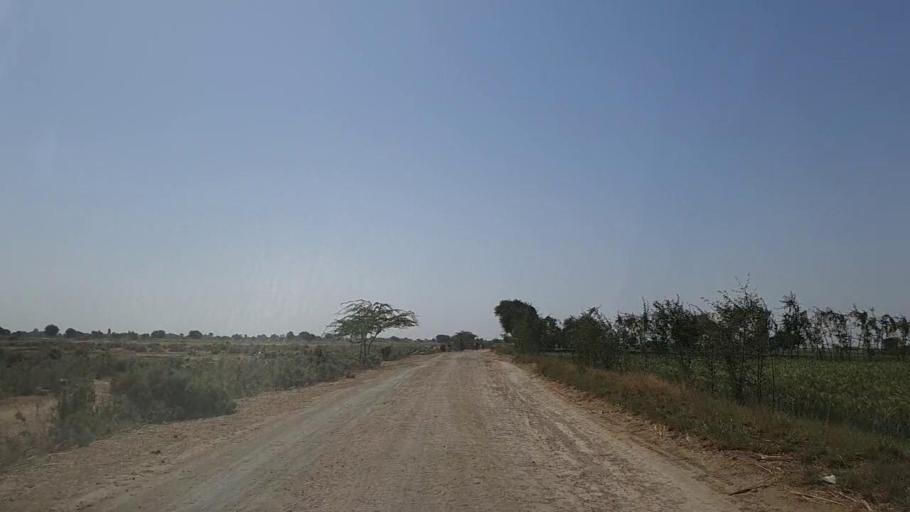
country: PK
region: Sindh
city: Samaro
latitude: 25.2297
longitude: 69.4077
